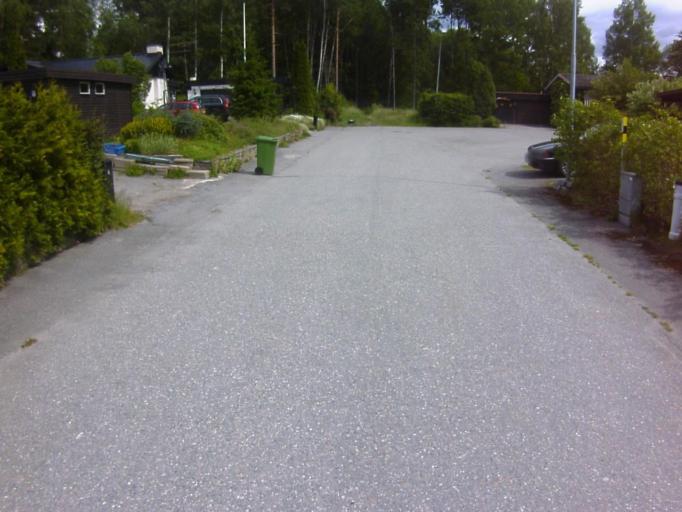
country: SE
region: Soedermanland
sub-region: Eskilstuna Kommun
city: Skogstorp
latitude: 59.3199
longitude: 16.4905
